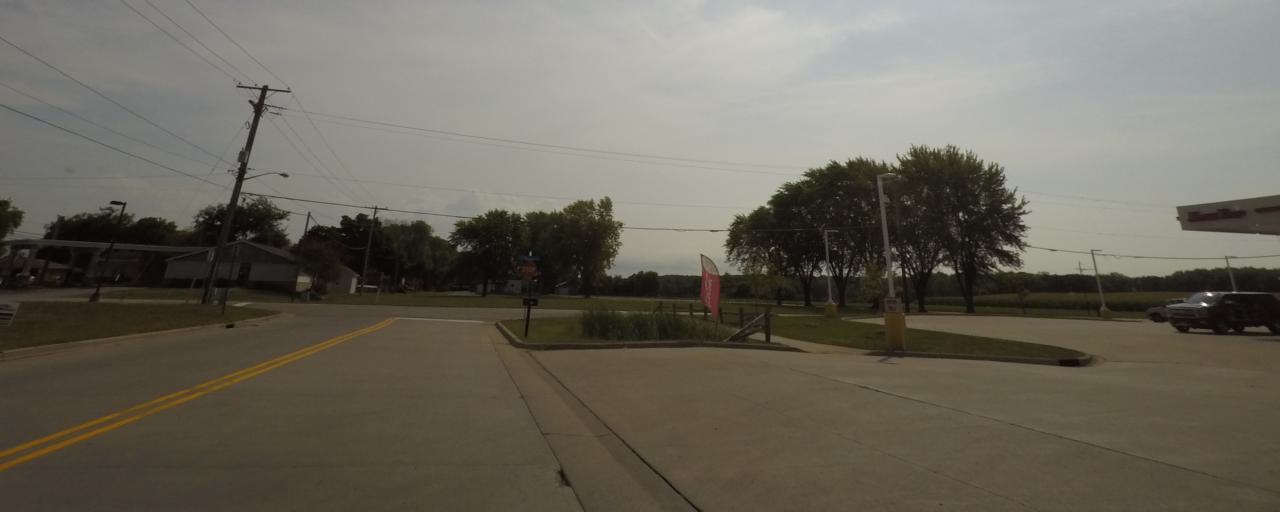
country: US
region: Wisconsin
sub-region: Jefferson County
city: Jefferson
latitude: 42.9908
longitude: -88.8076
